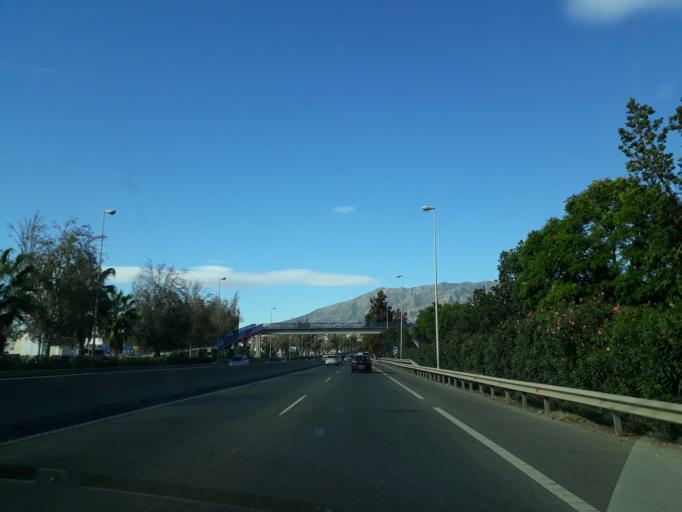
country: ES
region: Andalusia
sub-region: Provincia de Malaga
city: Fuengirola
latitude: 36.5354
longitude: -4.6332
